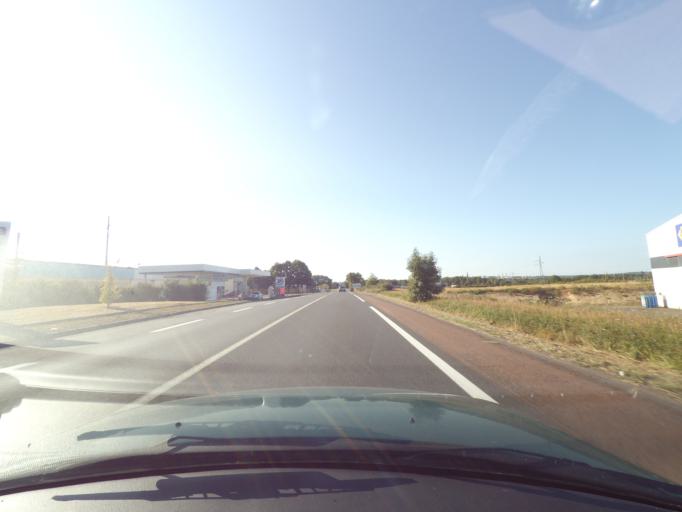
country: FR
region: Poitou-Charentes
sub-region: Departement des Deux-Sevres
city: Parthenay
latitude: 46.6675
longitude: -0.2538
